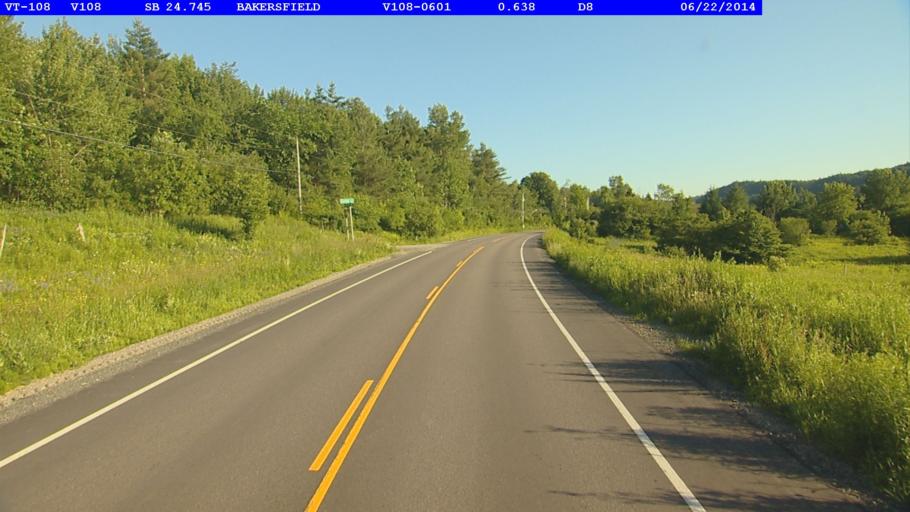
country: US
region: Vermont
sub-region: Franklin County
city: Enosburg Falls
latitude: 44.7423
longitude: -72.8233
